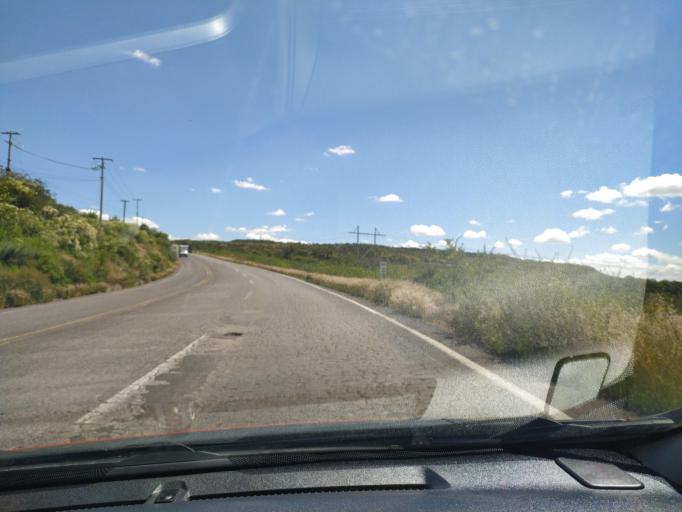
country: MX
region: Jalisco
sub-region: San Julian
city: Colonia Veintitres de Mayo
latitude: 21.0088
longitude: -102.2688
